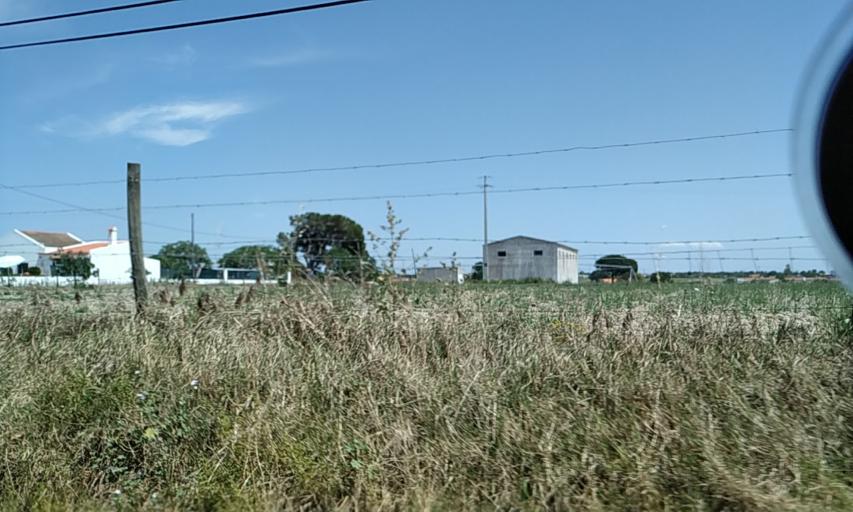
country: PT
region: Santarem
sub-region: Benavente
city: Poceirao
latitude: 38.6796
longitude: -8.7329
